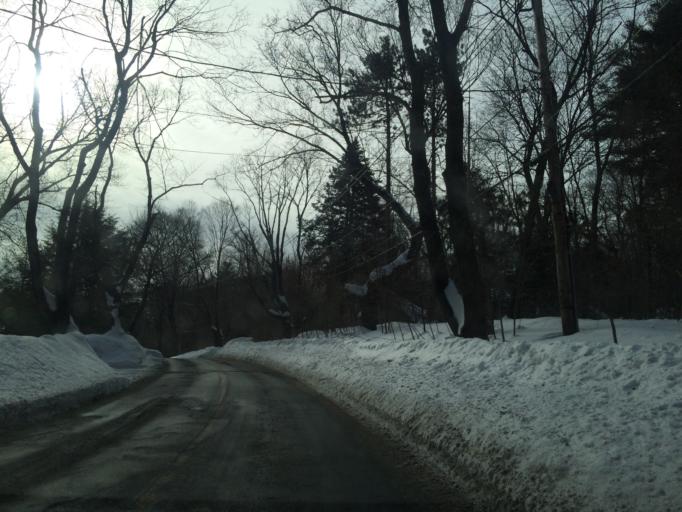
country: US
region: Massachusetts
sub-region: Middlesex County
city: Weston
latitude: 42.3602
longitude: -71.2743
